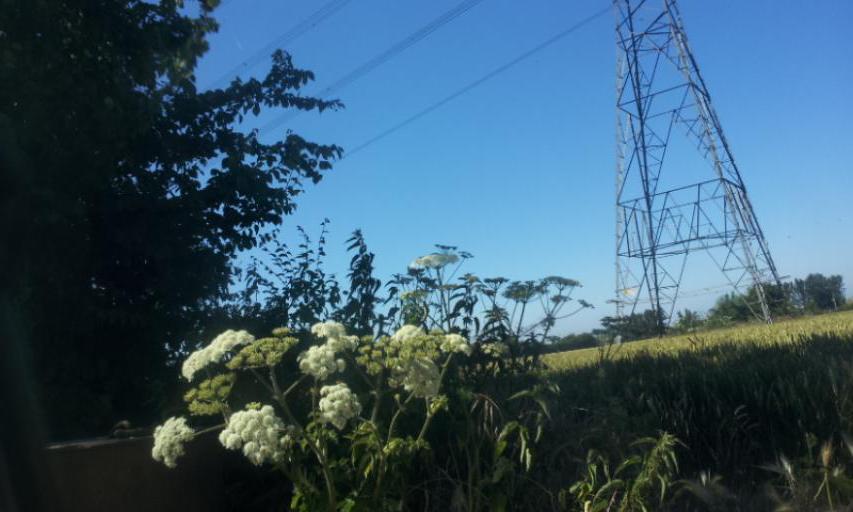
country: GB
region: England
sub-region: Kent
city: Teynham
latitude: 51.3537
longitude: 0.7764
